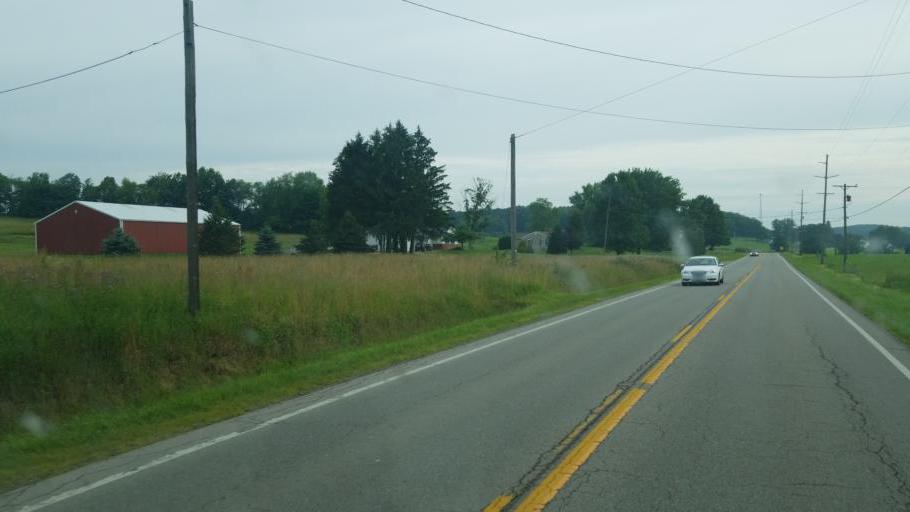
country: US
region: Ohio
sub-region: Sandusky County
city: Bellville
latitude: 40.5908
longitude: -82.5216
